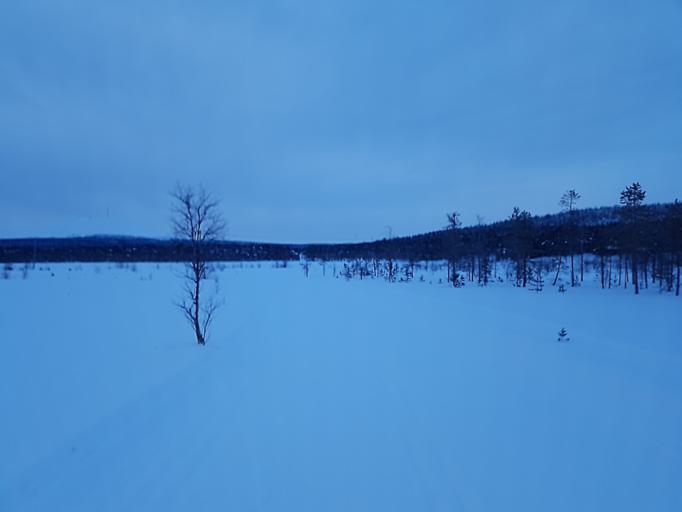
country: FI
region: Lapland
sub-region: Tunturi-Lappi
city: Kolari
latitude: 67.6178
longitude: 24.1314
